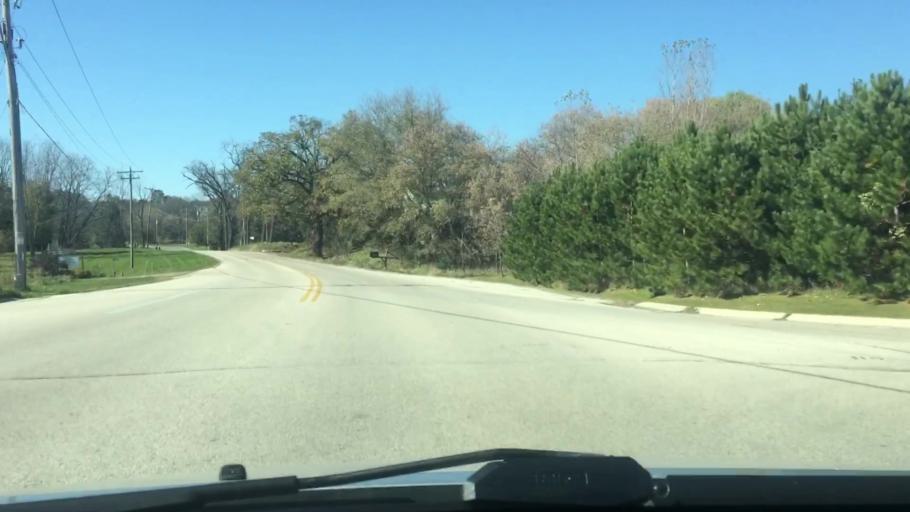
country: US
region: Wisconsin
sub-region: Waukesha County
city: Wales
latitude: 42.9916
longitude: -88.3670
